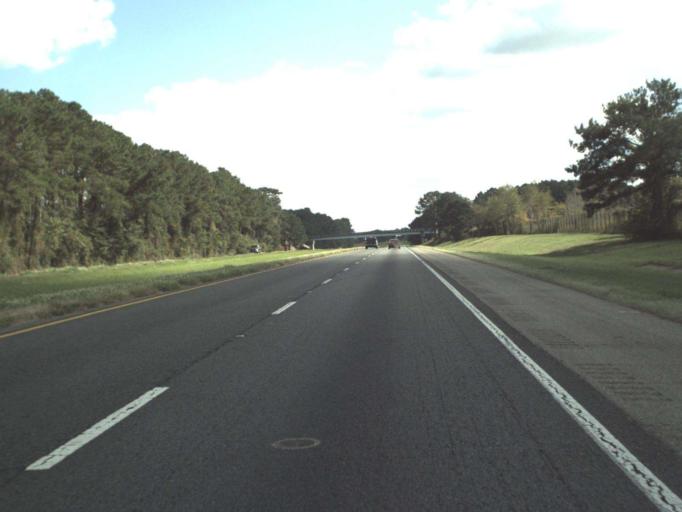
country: US
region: Florida
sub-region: Gadsden County
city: Gretna
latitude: 30.5991
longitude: -84.7271
